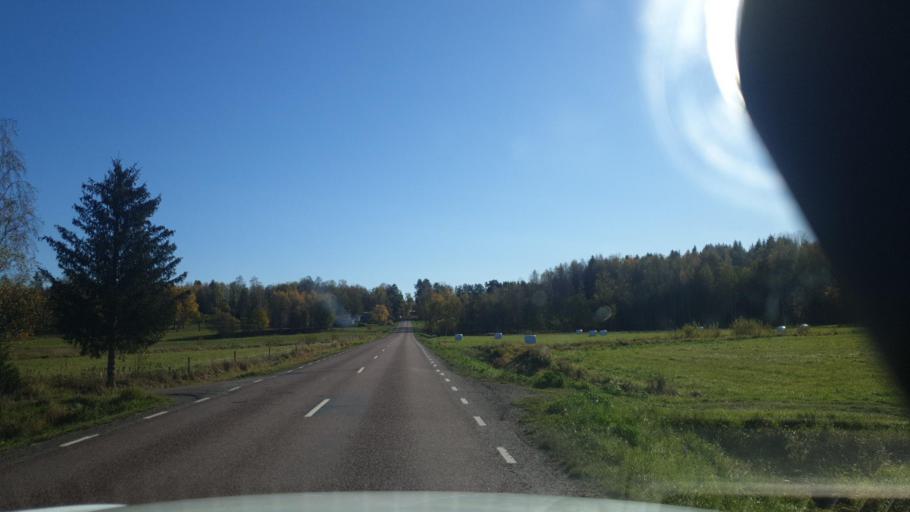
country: SE
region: Vaermland
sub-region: Grums Kommun
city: Grums
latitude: 59.4538
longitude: 12.9687
